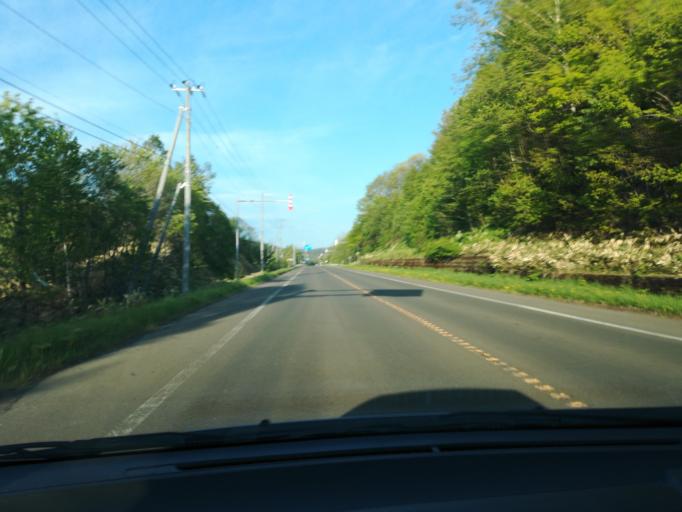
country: JP
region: Hokkaido
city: Shimo-furano
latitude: 43.1390
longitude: 142.6180
